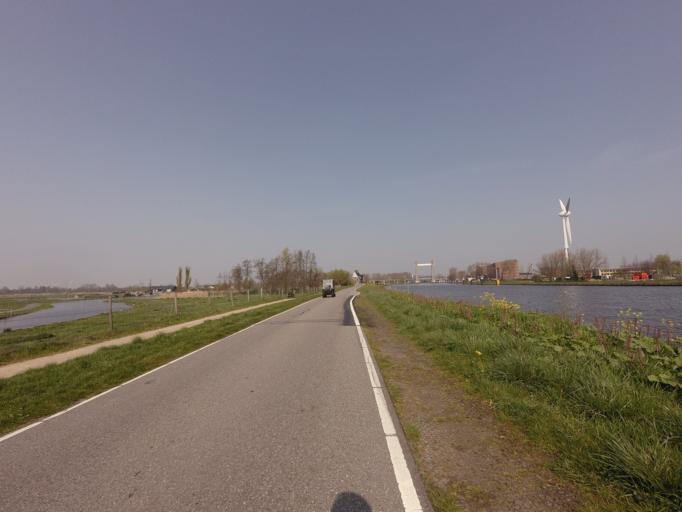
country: NL
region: South Holland
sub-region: Gemeente Gouda
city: Bloemendaal
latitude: 52.0120
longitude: 4.6849
